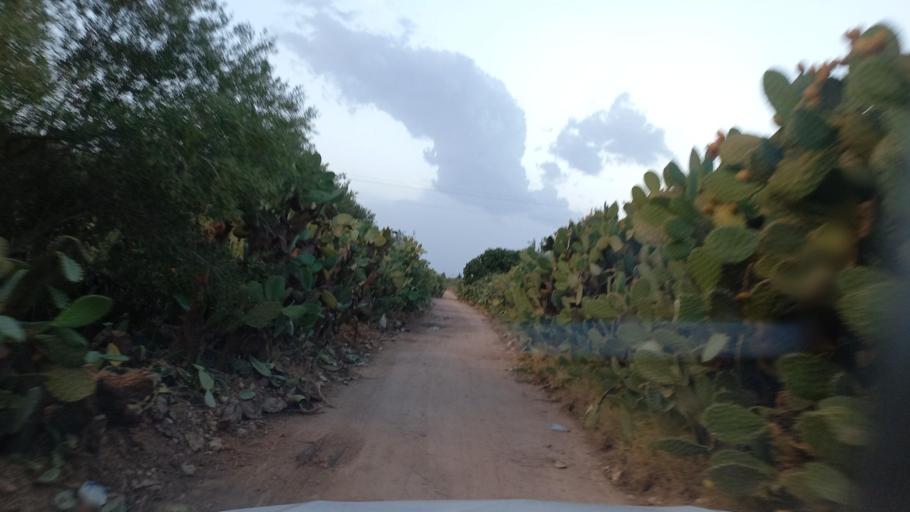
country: TN
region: Al Qasrayn
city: Kasserine
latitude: 35.2802
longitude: 9.0498
